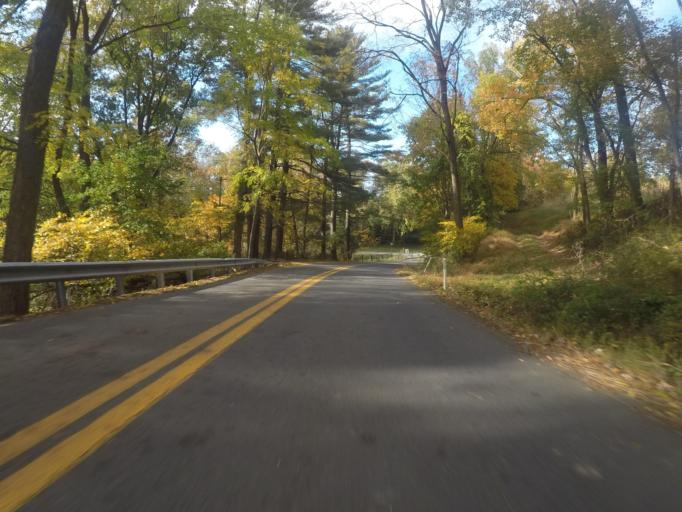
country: US
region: Maryland
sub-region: Baltimore County
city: Reisterstown
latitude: 39.5321
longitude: -76.8618
